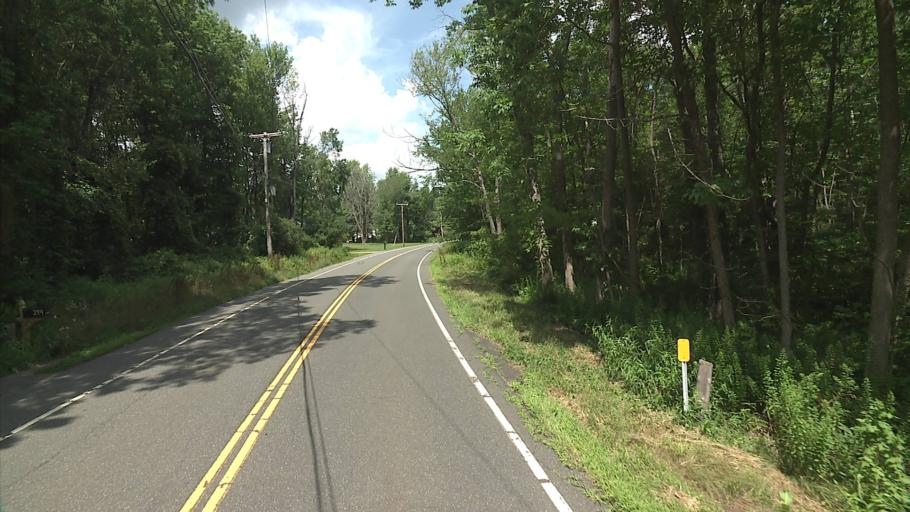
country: US
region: Massachusetts
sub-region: Hampden County
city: Granville
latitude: 42.0132
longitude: -72.9709
